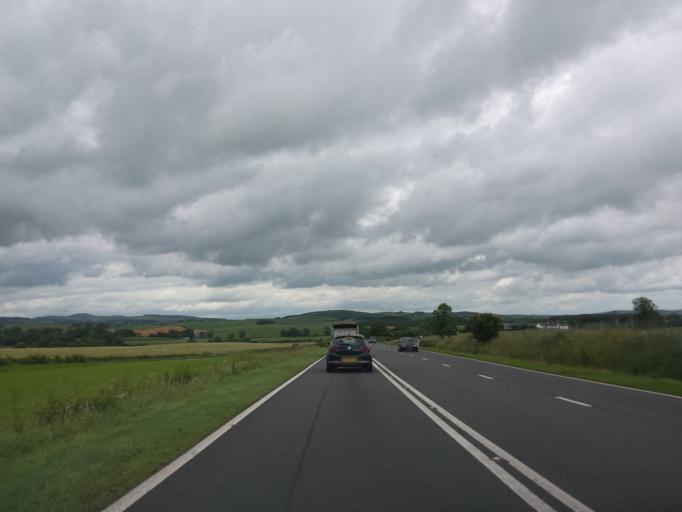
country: GB
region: Scotland
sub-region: Dumfries and Galloway
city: Castle Douglas
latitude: 54.9701
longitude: -3.9011
